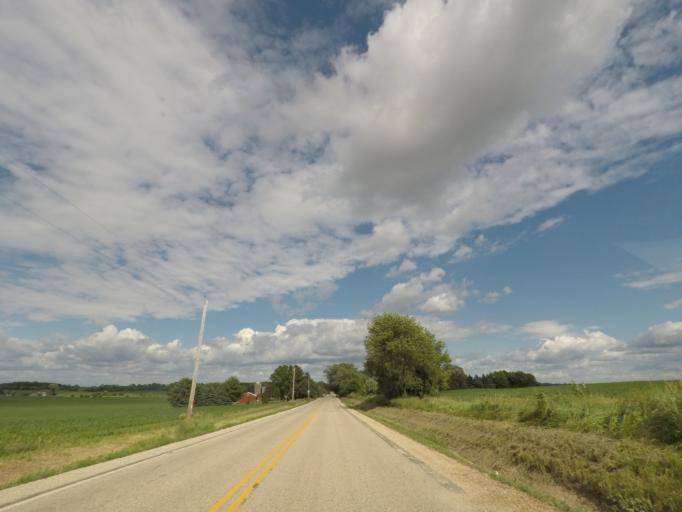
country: US
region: Wisconsin
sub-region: Rock County
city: Orfordville
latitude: 42.7086
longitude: -89.1795
